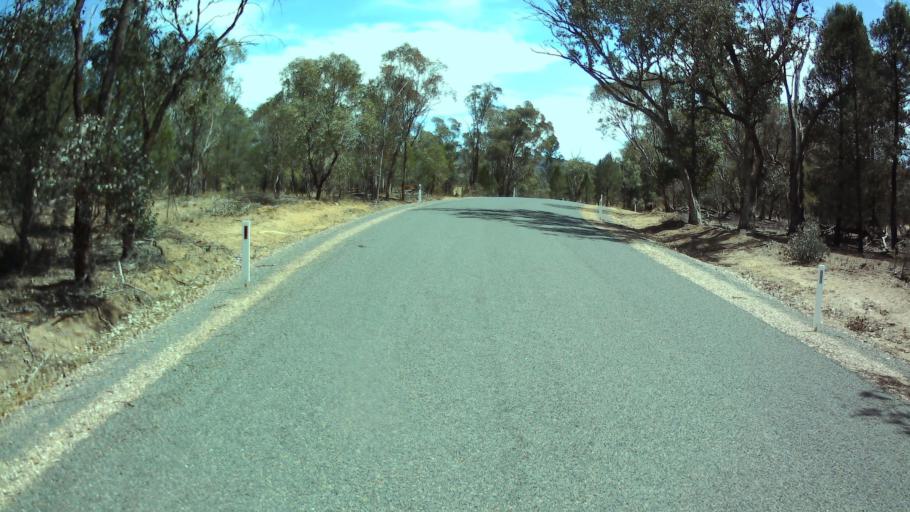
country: AU
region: New South Wales
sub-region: Weddin
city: Grenfell
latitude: -33.7684
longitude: 148.2045
